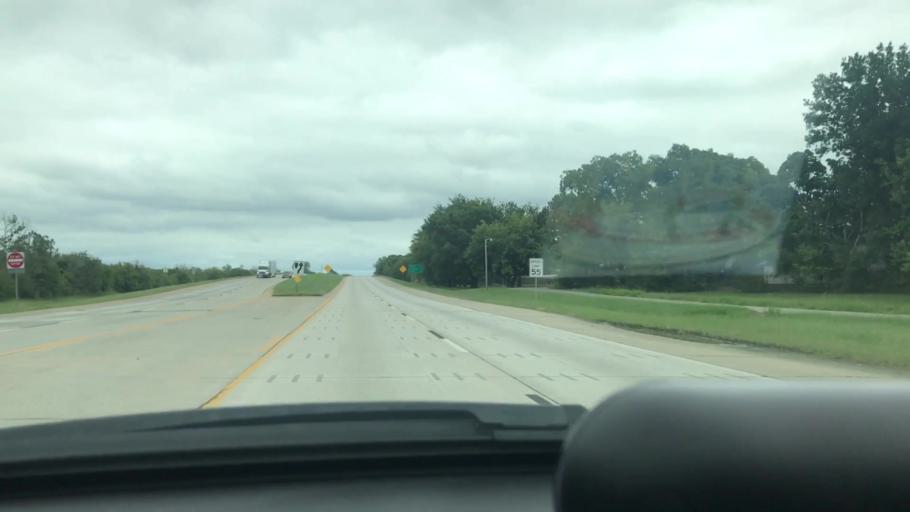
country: US
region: Oklahoma
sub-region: Wagoner County
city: Wagoner
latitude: 35.9659
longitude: -95.3911
